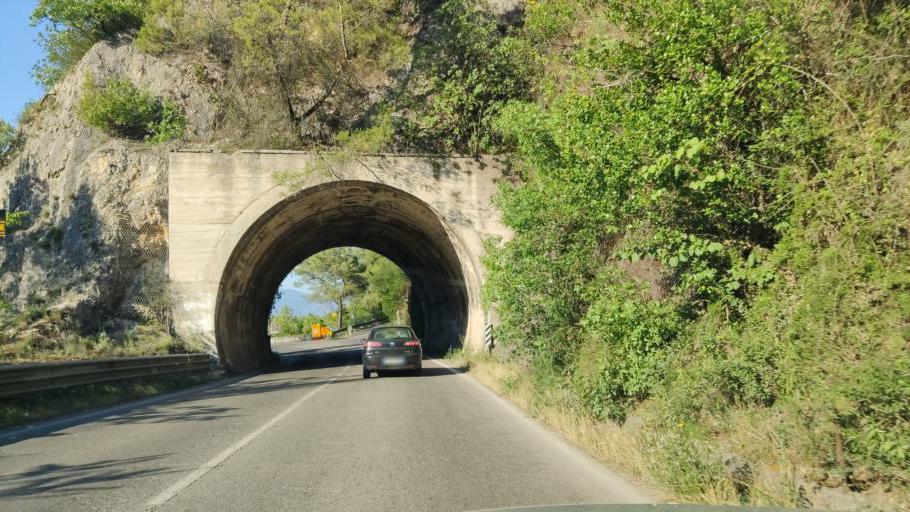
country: IT
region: Umbria
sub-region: Provincia di Terni
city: Narni Scalo
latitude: 42.5238
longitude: 12.5121
